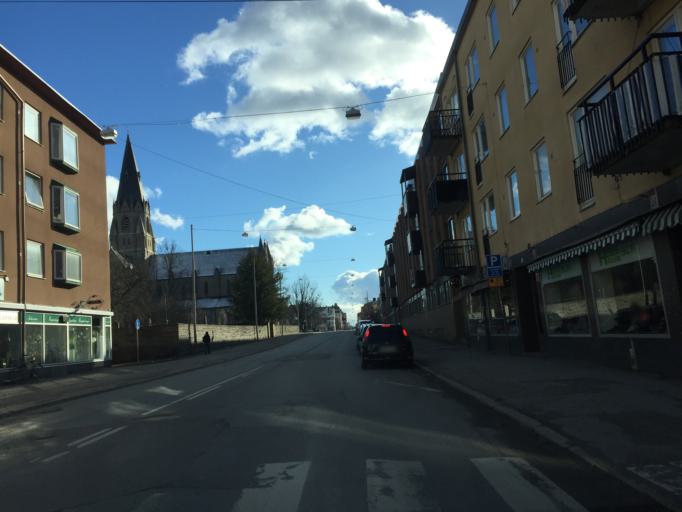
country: SE
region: OErebro
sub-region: Orebro Kommun
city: Orebro
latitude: 59.2817
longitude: 15.2197
